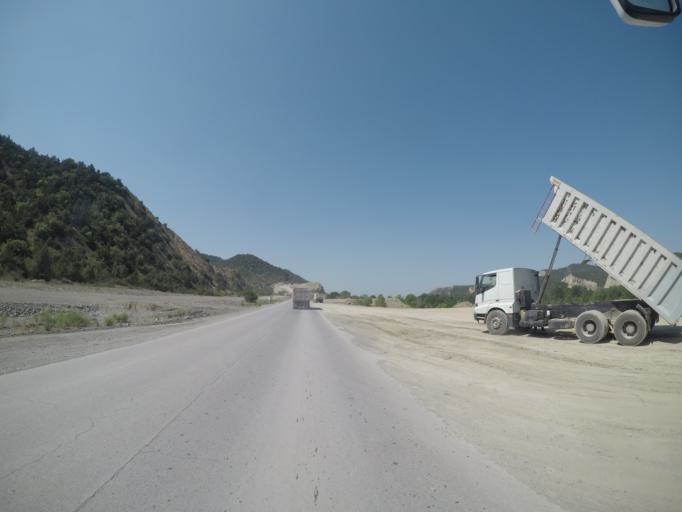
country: AZ
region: Agdas
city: Agdas
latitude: 40.7272
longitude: 47.5674
